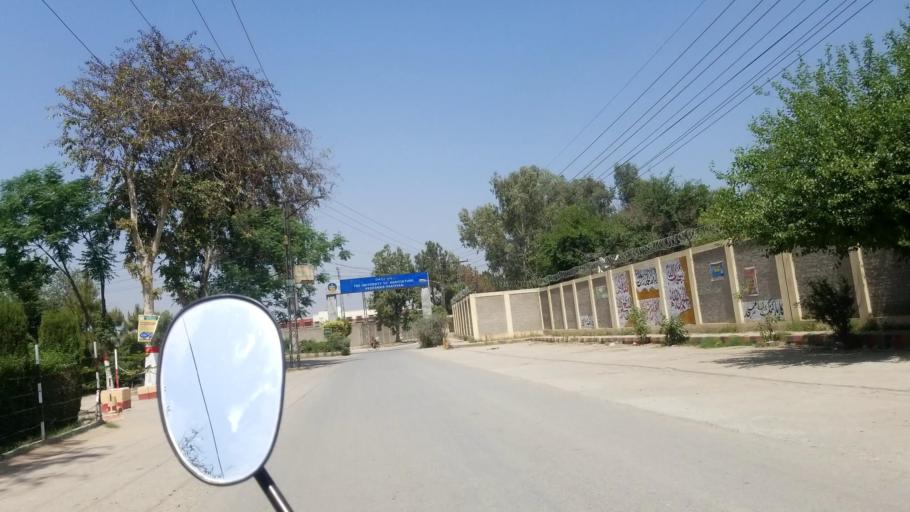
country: PK
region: Khyber Pakhtunkhwa
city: Peshawar
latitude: 34.0188
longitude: 71.4837
